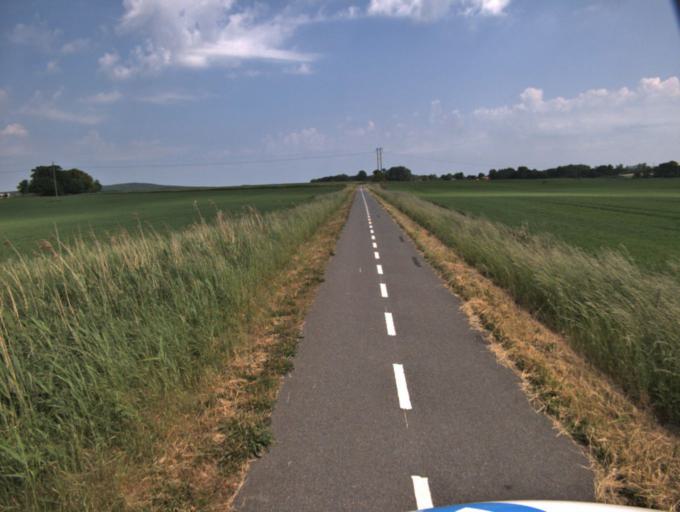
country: SE
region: Skane
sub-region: Kristianstads Kommun
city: Kristianstad
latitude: 56.0675
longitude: 14.1931
